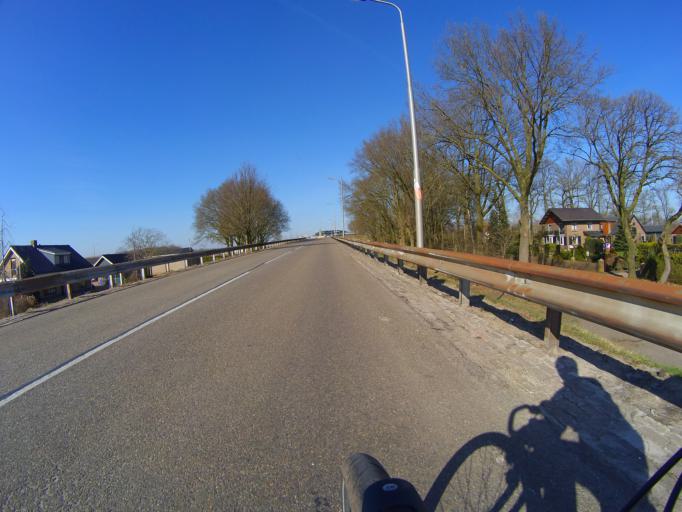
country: NL
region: Utrecht
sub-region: Gemeente Leusden
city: Leusden
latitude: 52.1642
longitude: 5.4590
